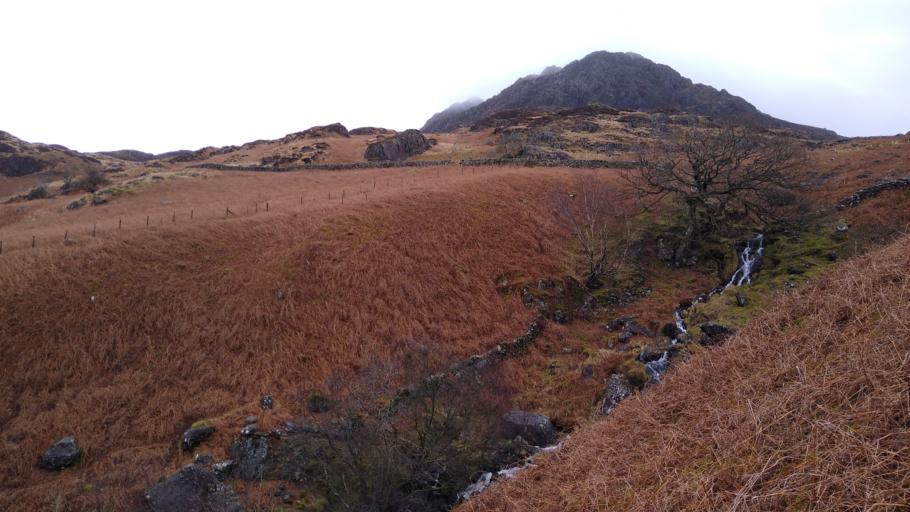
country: GB
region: England
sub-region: Cumbria
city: Millom
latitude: 54.3915
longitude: -3.2250
